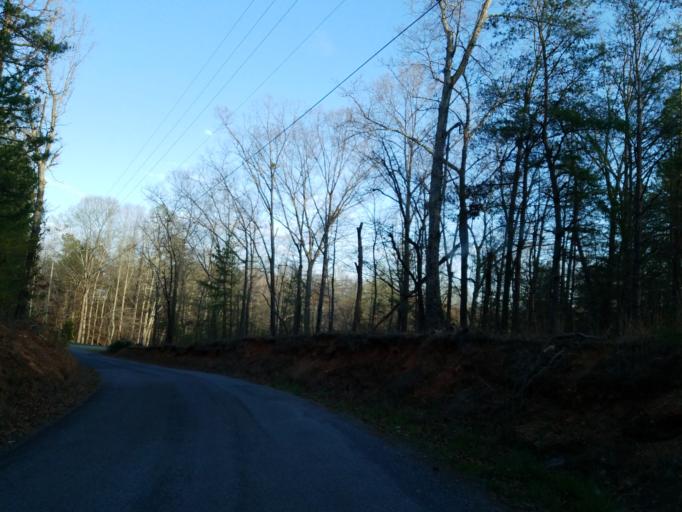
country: US
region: Georgia
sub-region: Pickens County
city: Jasper
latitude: 34.5124
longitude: -84.6179
